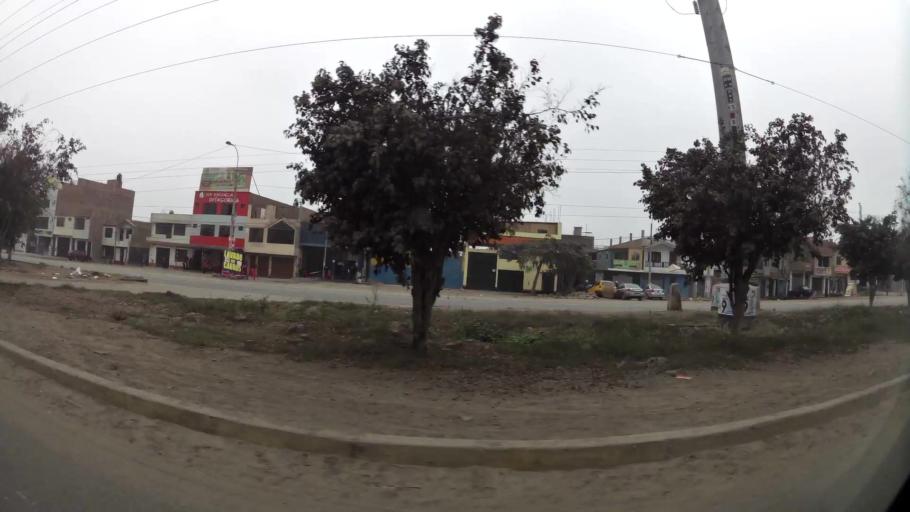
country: PE
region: Lima
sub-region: Lima
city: Urb. Santo Domingo
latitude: -11.8906
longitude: -77.0442
